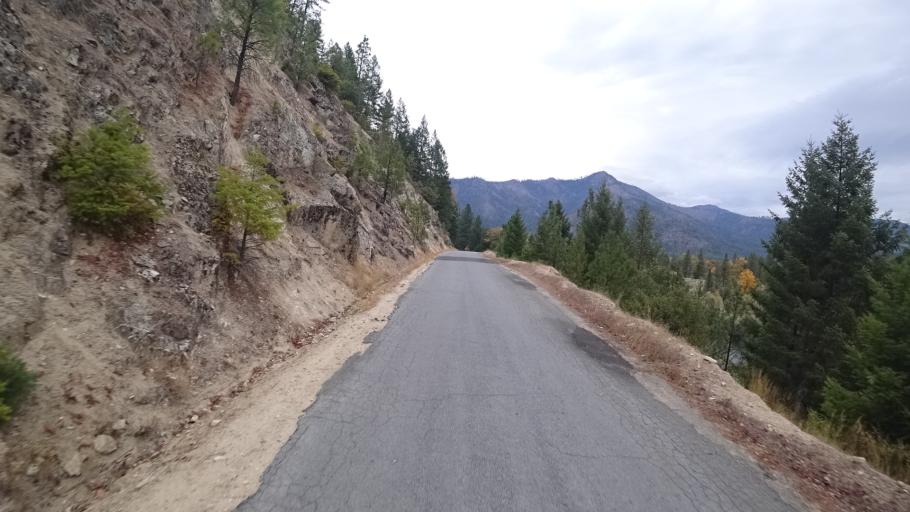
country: US
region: California
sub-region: Siskiyou County
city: Happy Camp
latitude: 41.8301
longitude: -123.1951
